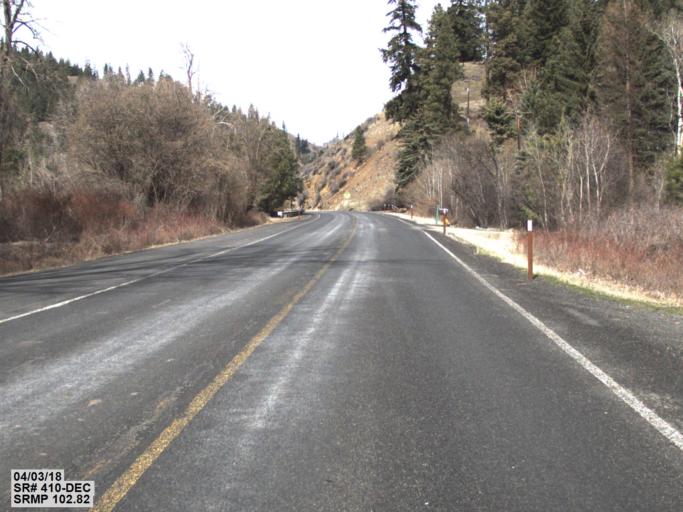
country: US
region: Washington
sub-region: Yakima County
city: Tieton
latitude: 46.8746
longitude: -120.9758
